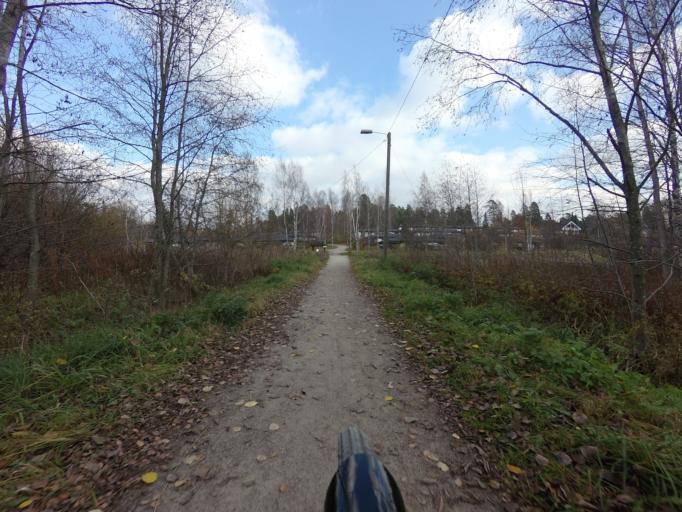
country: FI
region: Uusimaa
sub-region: Helsinki
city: Kauniainen
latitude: 60.1724
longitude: 24.7015
